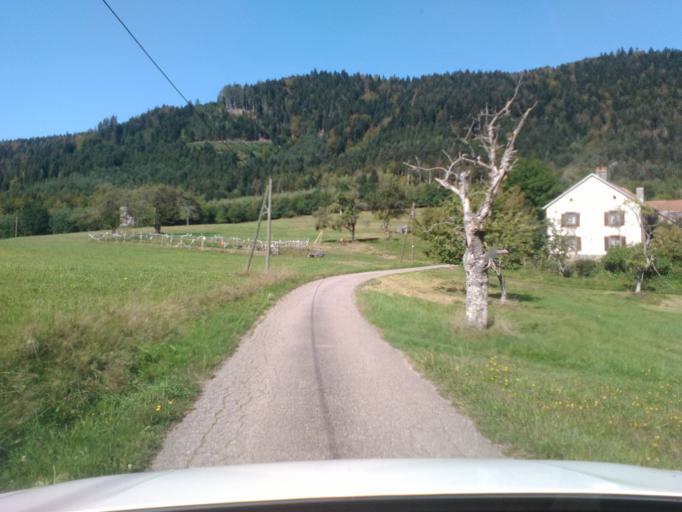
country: FR
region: Lorraine
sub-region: Departement des Vosges
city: Senones
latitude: 48.4137
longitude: 6.9915
